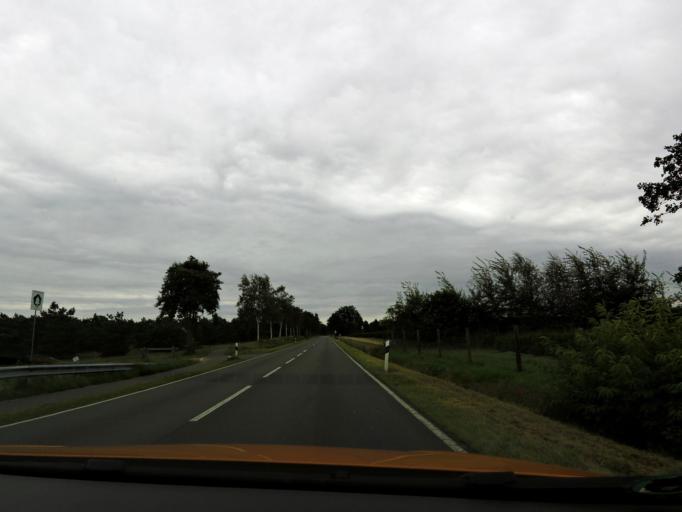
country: DE
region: Lower Saxony
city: Westerstede
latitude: 53.2505
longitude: 7.9721
